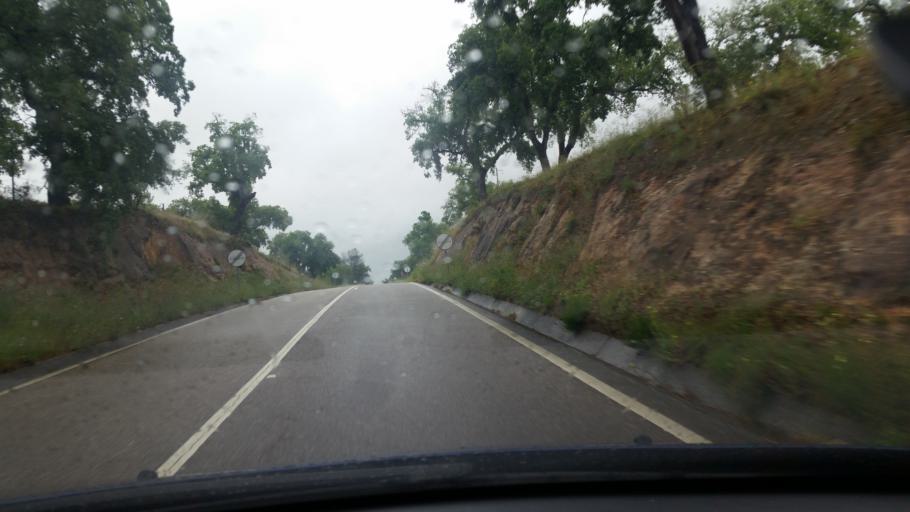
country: PT
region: Portalegre
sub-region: Avis
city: Avis
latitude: 39.1216
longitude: -7.9731
